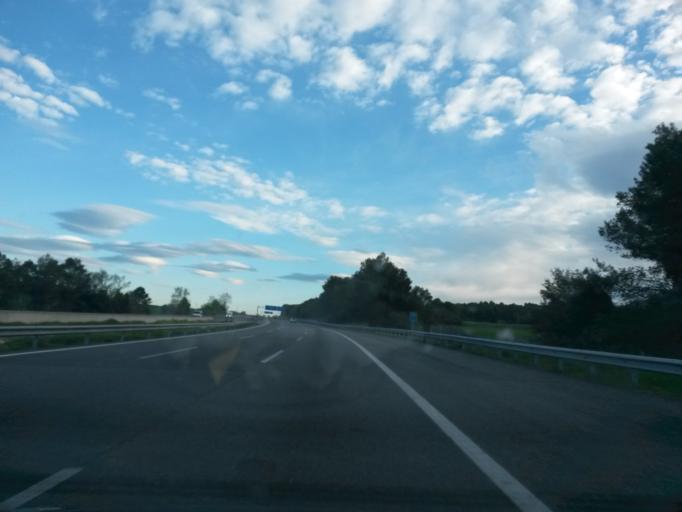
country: ES
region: Catalonia
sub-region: Provincia de Girona
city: Vilademuls
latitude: 42.1137
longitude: 2.9134
